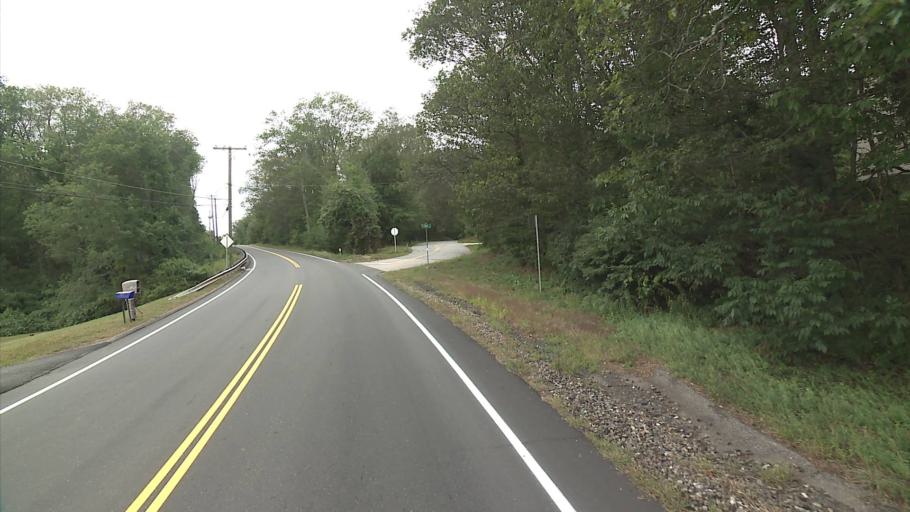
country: US
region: Connecticut
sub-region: Tolland County
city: Hebron
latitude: 41.6394
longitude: -72.3479
